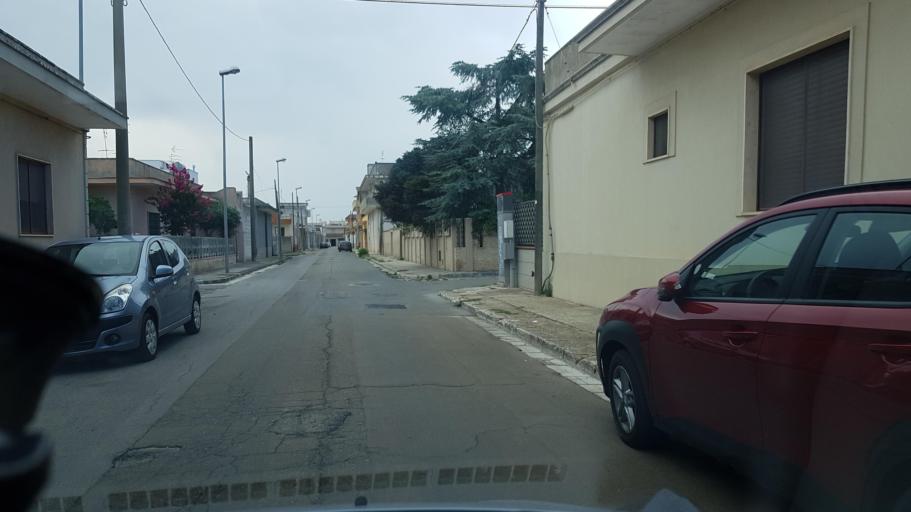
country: IT
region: Apulia
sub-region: Provincia di Brindisi
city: Mesagne
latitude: 40.5494
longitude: 17.8105
